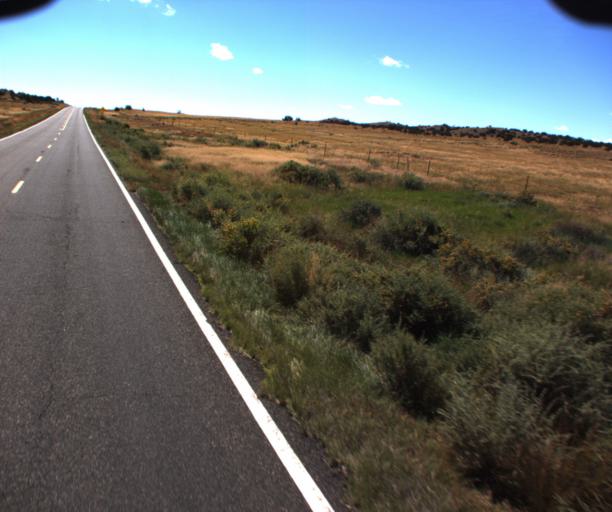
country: US
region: Arizona
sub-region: Apache County
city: Saint Johns
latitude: 34.7607
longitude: -109.2425
